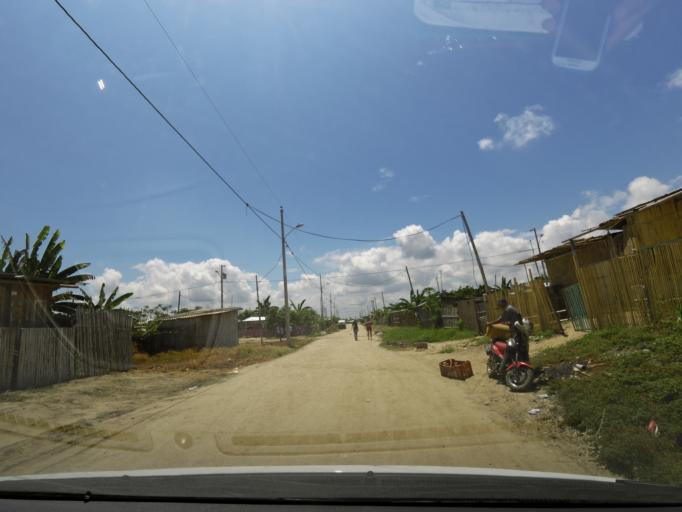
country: EC
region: El Oro
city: Huaquillas
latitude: -3.4733
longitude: -80.2107
